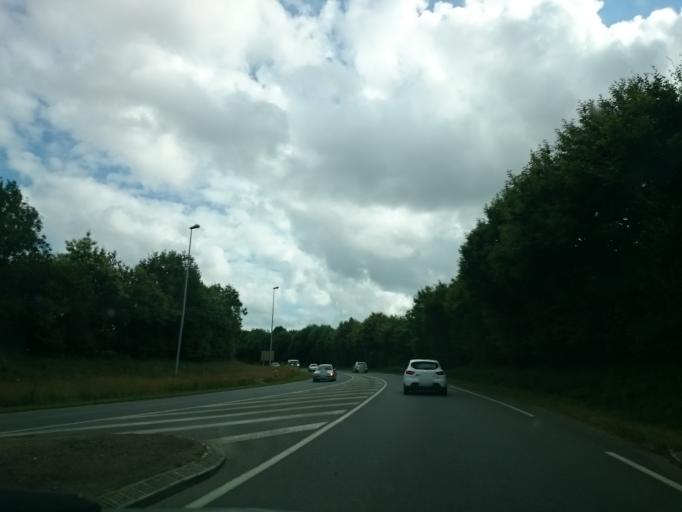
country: FR
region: Brittany
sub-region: Departement du Finistere
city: Gouesnou
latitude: 48.4434
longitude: -4.4571
